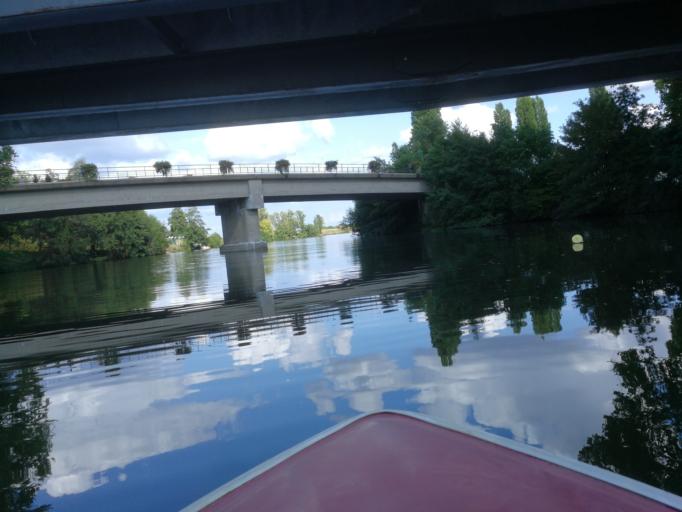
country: FR
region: Centre
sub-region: Departement d'Indre-et-Loire
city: Saint-Avertin
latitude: 47.3695
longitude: 0.7235
